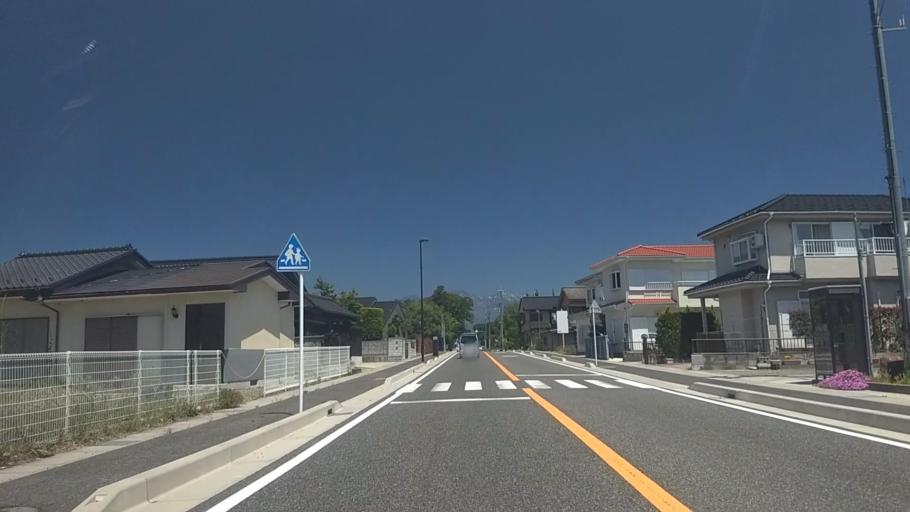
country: JP
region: Yamanashi
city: Nirasaki
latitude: 35.7564
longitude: 138.4333
